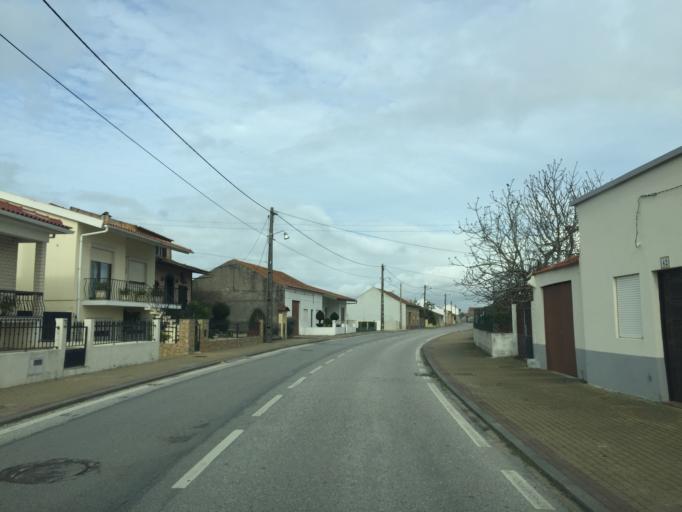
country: PT
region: Coimbra
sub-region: Figueira da Foz
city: Lavos
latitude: 40.0567
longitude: -8.8144
